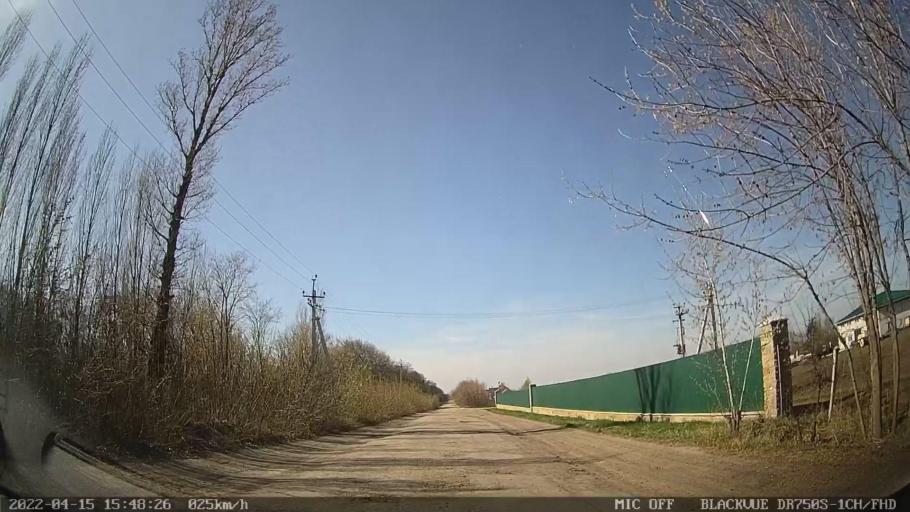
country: MD
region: Raionul Ocnita
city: Otaci
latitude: 48.3869
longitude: 27.9069
